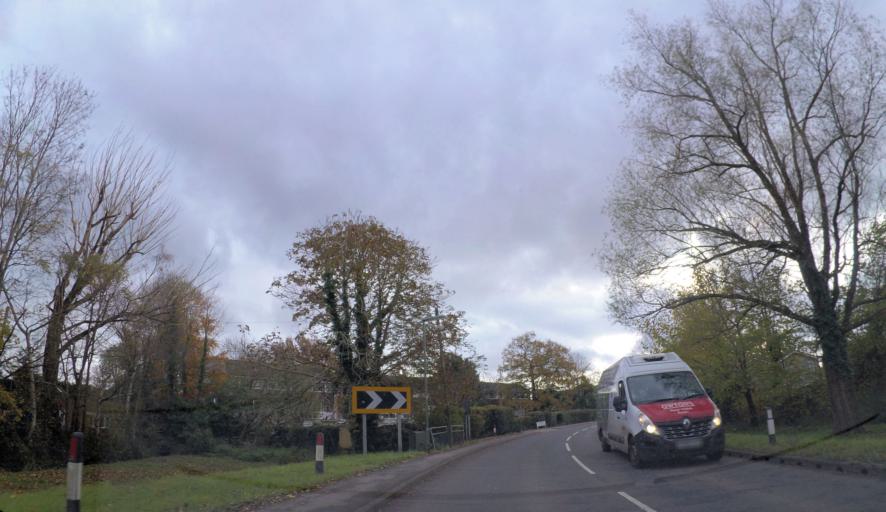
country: GB
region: England
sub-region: Surrey
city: Salfords
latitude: 51.2170
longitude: -0.1756
